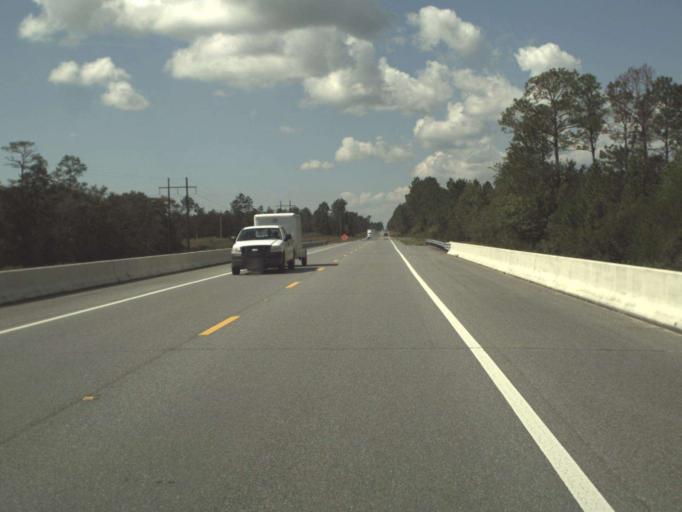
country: US
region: Florida
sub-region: Walton County
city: Freeport
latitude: 30.4741
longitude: -85.9885
